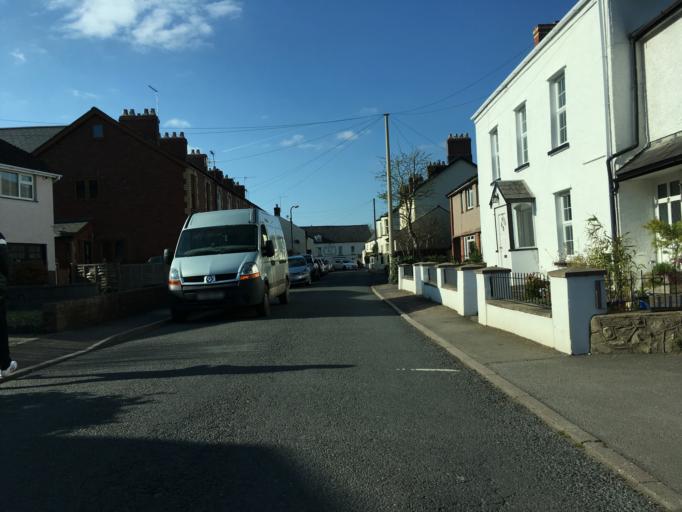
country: GB
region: Wales
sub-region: Monmouthshire
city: Llanbadoc
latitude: 51.6992
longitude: -2.9034
